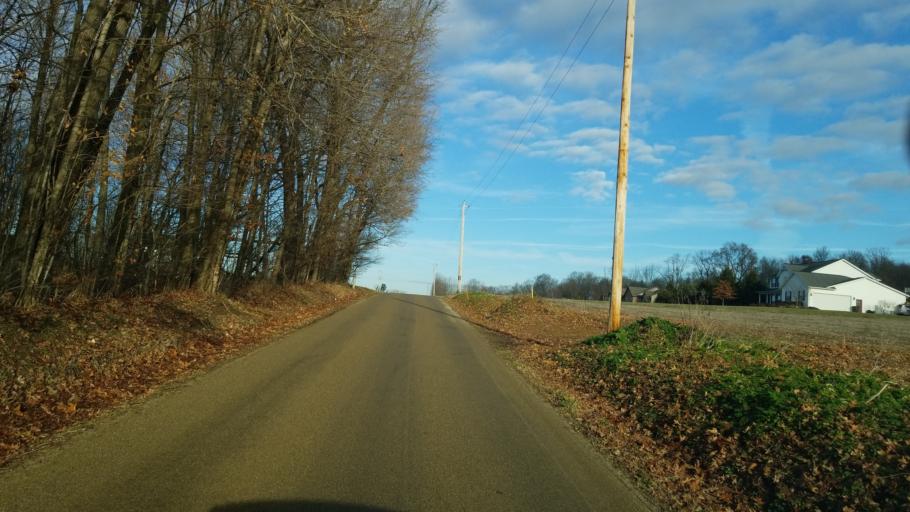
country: US
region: Ohio
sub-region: Knox County
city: Gambier
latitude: 40.3257
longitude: -82.3796
